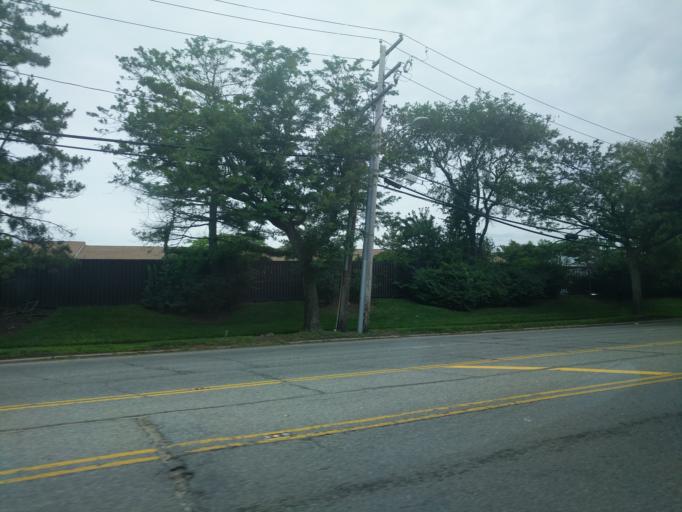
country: US
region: New York
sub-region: Nassau County
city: Barnum Island
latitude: 40.6206
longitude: -73.6445
